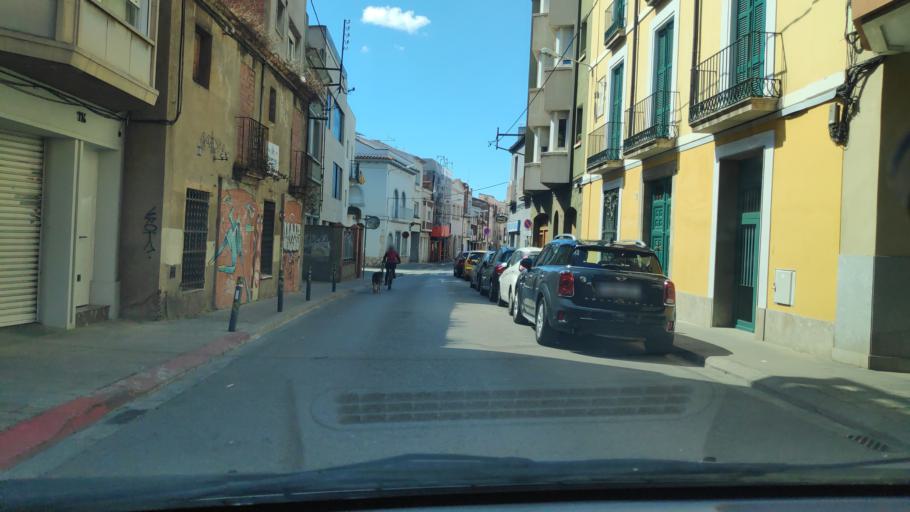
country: ES
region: Catalonia
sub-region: Provincia de Barcelona
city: Sabadell
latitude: 41.5518
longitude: 2.1115
